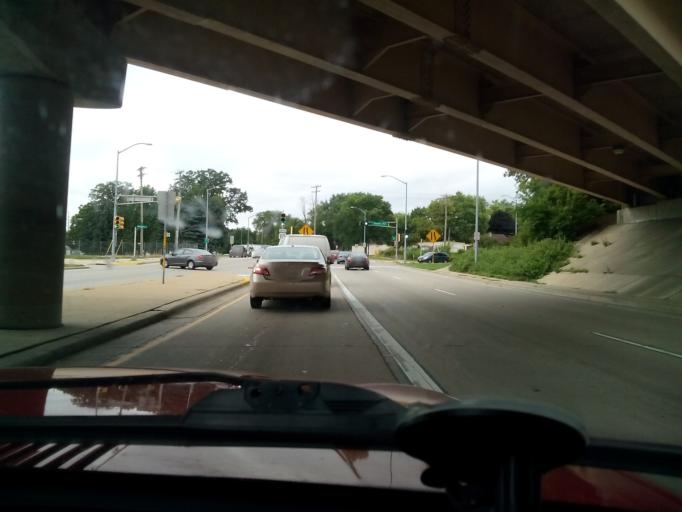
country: US
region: Wisconsin
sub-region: Dane County
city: Maple Bluff
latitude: 43.1133
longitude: -89.3543
